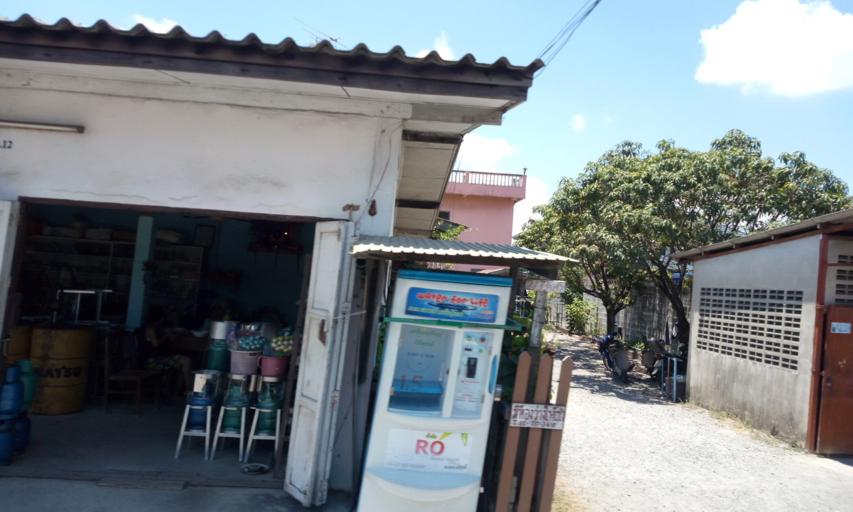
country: TH
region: Bangkok
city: Bang Na
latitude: 13.6093
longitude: 100.7059
